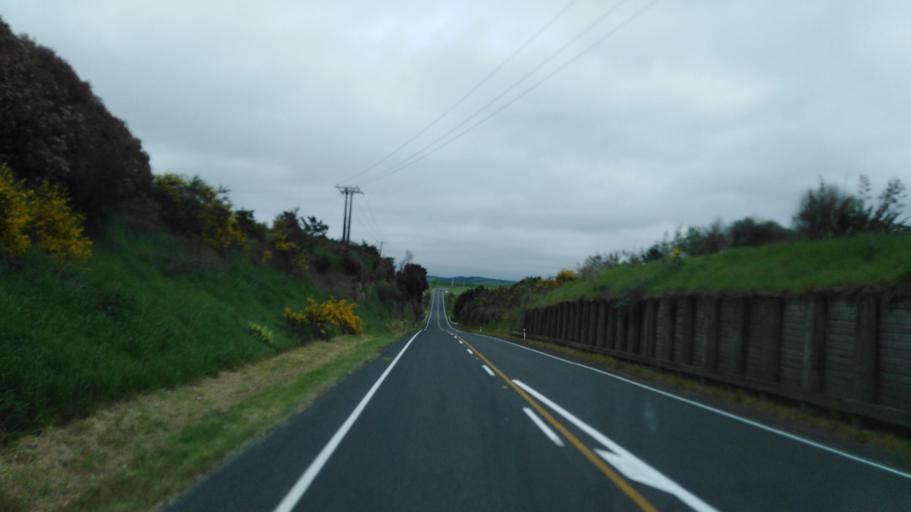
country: NZ
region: Waikato
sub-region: Taupo District
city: Taupo
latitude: -38.6140
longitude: 176.2621
